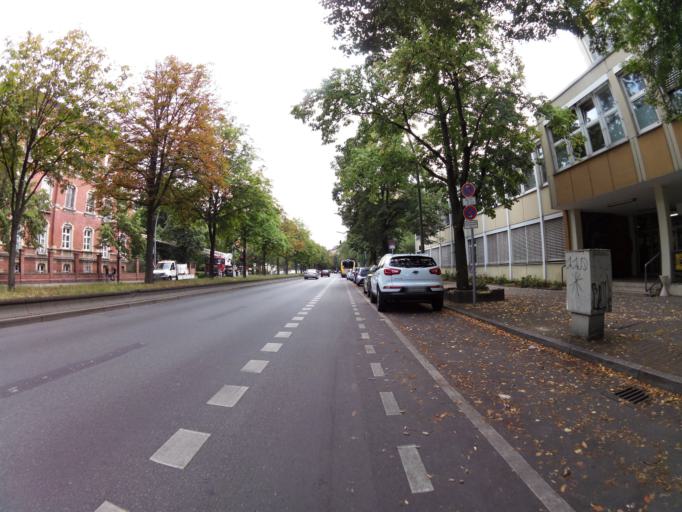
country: DE
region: Berlin
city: Wedding Bezirk
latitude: 52.5556
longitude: 13.3657
